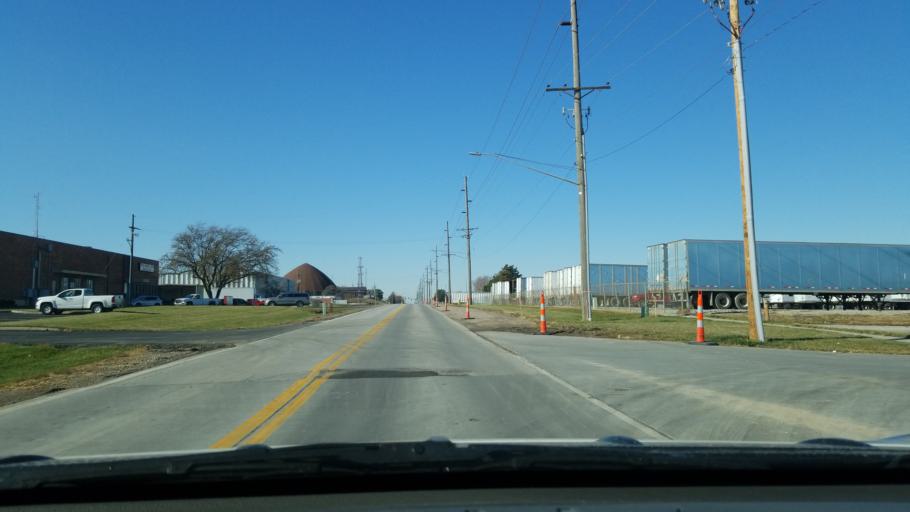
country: US
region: Nebraska
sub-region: Douglas County
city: Ralston
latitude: 41.2163
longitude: -96.0740
